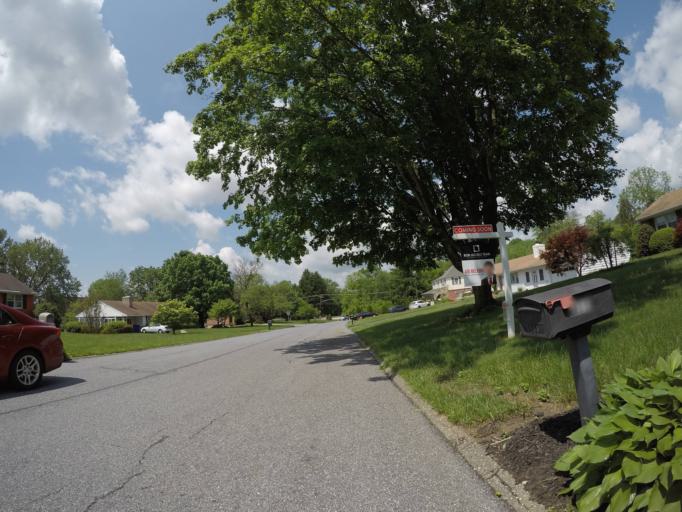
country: US
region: Maryland
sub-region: Howard County
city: Columbia
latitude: 39.2939
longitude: -76.8551
